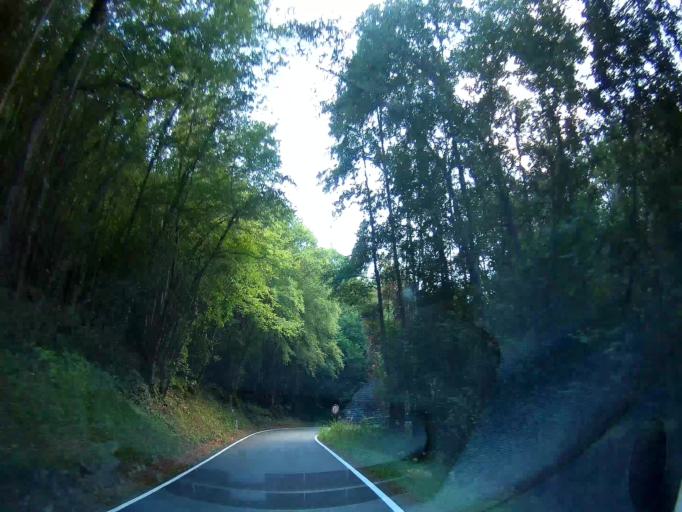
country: BE
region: Wallonia
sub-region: Province de Namur
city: Onhaye
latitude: 50.3010
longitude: 4.7776
